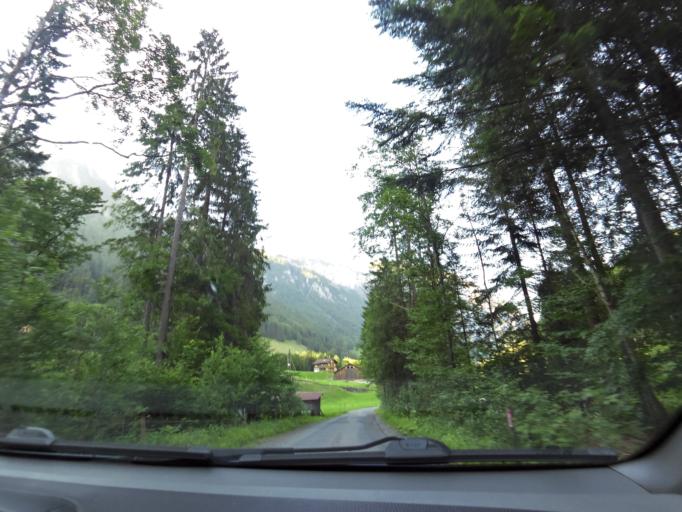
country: CH
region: Nidwalden
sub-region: Nidwalden
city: Emmetten
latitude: 46.9036
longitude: 8.5236
